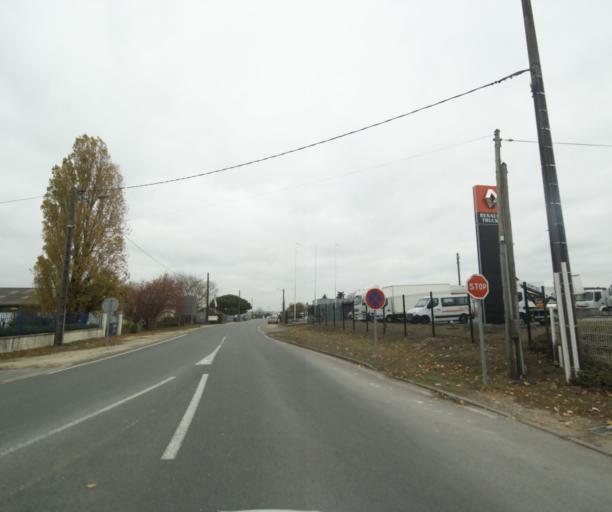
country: FR
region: Poitou-Charentes
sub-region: Departement de la Charente-Maritime
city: Les Gonds
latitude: 45.7207
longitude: -0.6436
